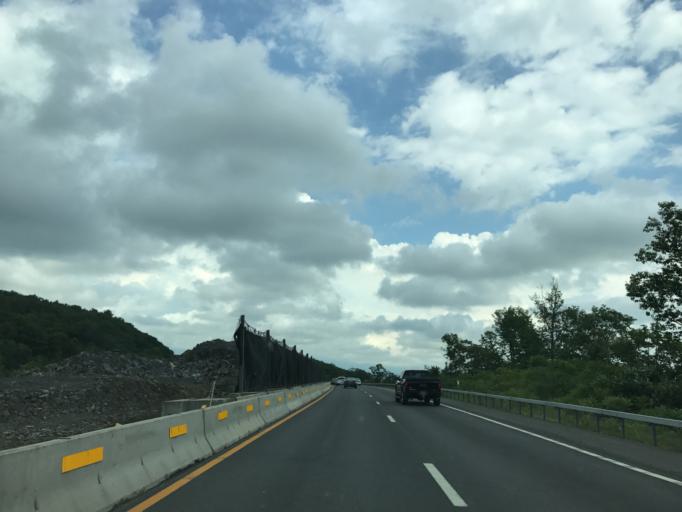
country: US
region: New York
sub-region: Greene County
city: Jefferson Heights
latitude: 42.2766
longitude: -73.8728
